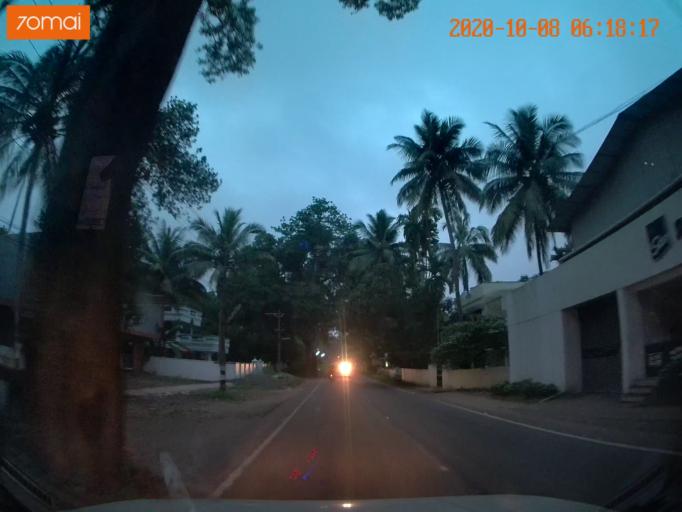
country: IN
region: Kerala
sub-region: Thrissur District
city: Trichur
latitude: 10.5122
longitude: 76.2489
